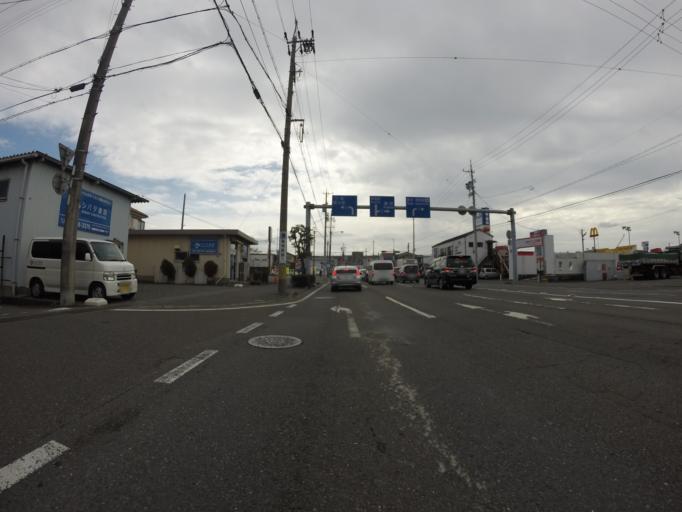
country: JP
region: Shizuoka
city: Shizuoka-shi
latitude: 35.0149
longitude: 138.4464
